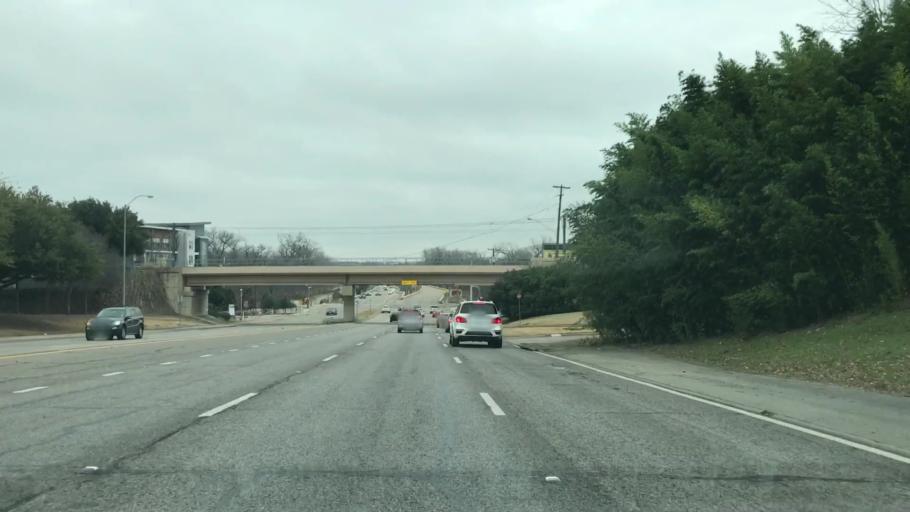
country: US
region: Texas
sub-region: Dallas County
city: Highland Park
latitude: 32.8546
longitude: -96.7337
